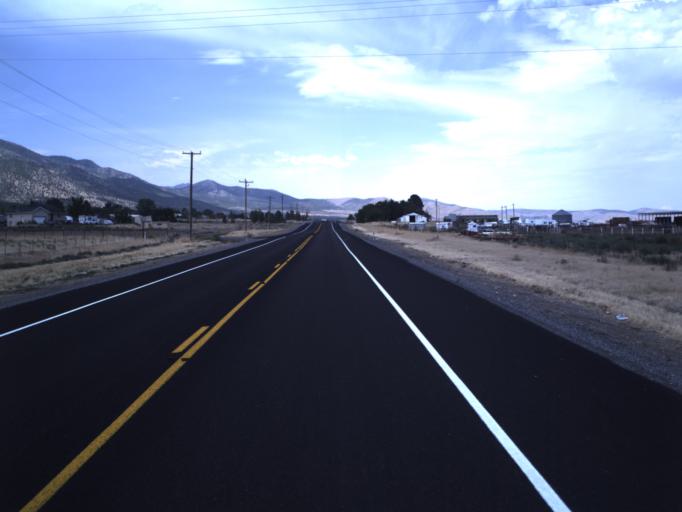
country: US
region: Utah
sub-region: Utah County
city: Eagle Mountain
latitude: 40.2911
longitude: -112.0977
